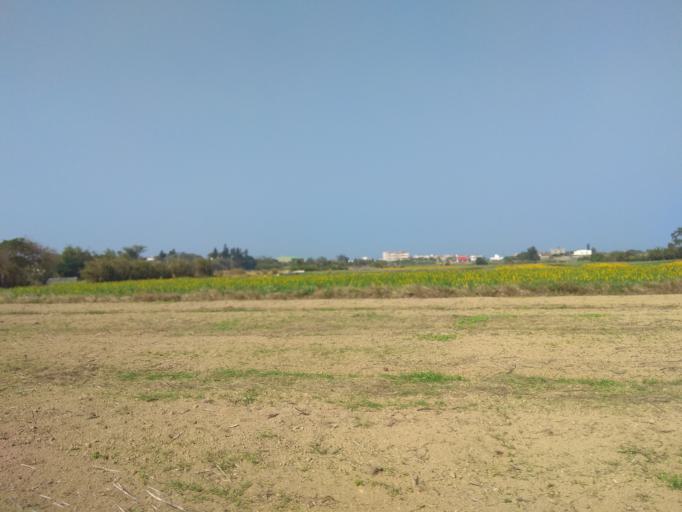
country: TW
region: Taiwan
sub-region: Hsinchu
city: Zhubei
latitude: 24.9965
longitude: 121.0410
